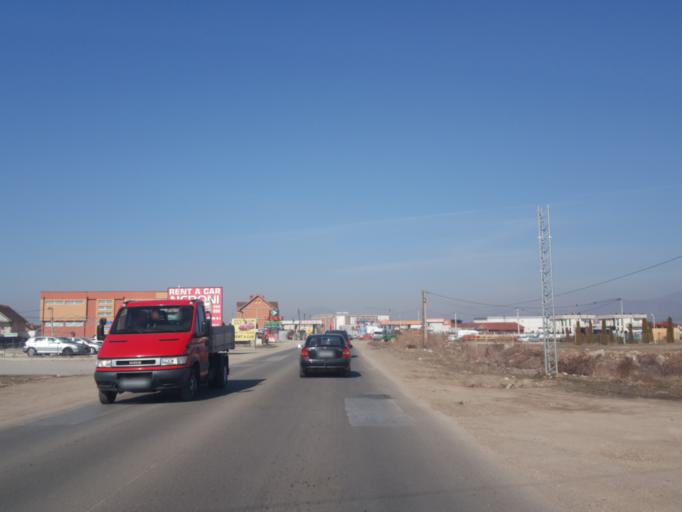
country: XK
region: Mitrovica
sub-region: Vushtrri
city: Vushtrri
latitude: 42.8118
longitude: 20.9857
